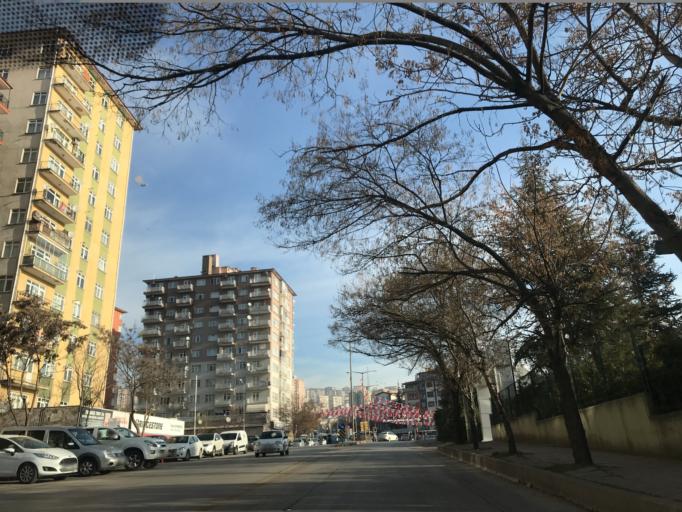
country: TR
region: Ankara
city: Batikent
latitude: 39.9633
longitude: 32.7975
